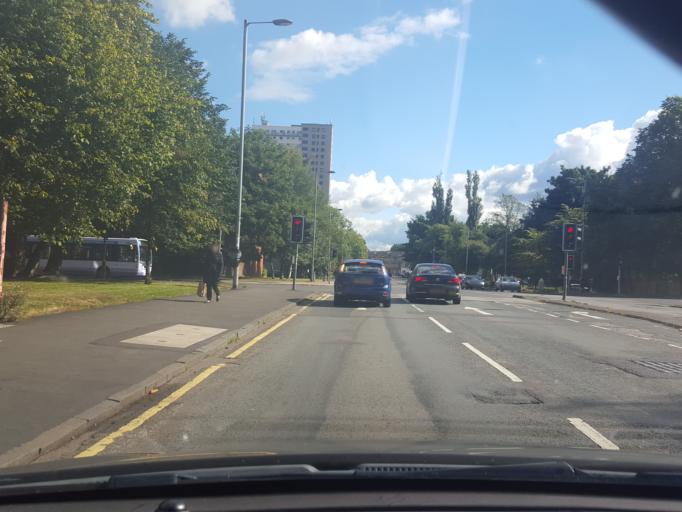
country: GB
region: Scotland
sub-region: East Renfrewshire
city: Giffnock
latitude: 55.8520
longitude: -4.3071
